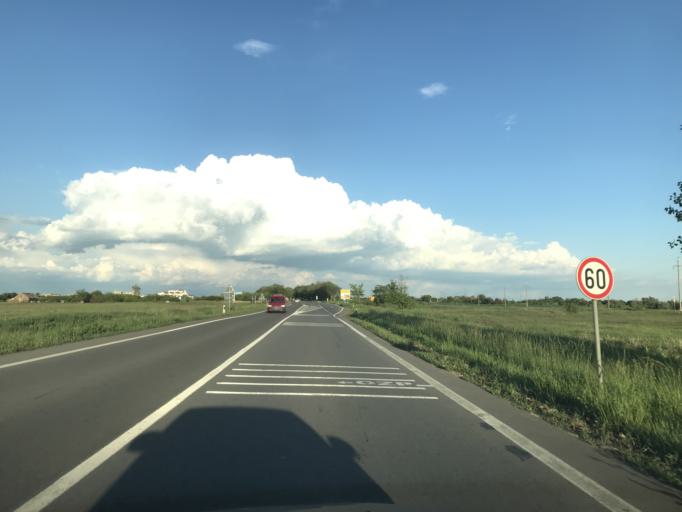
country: RS
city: Aradac
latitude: 45.3820
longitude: 20.3344
